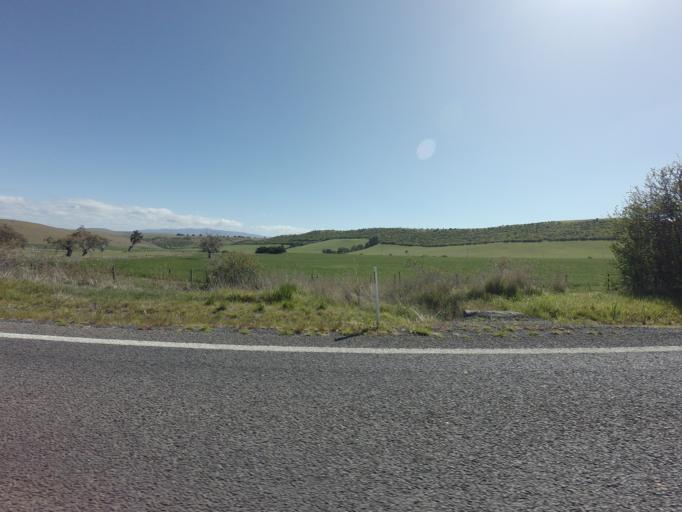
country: AU
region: Tasmania
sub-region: Derwent Valley
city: New Norfolk
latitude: -42.5682
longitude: 146.8808
